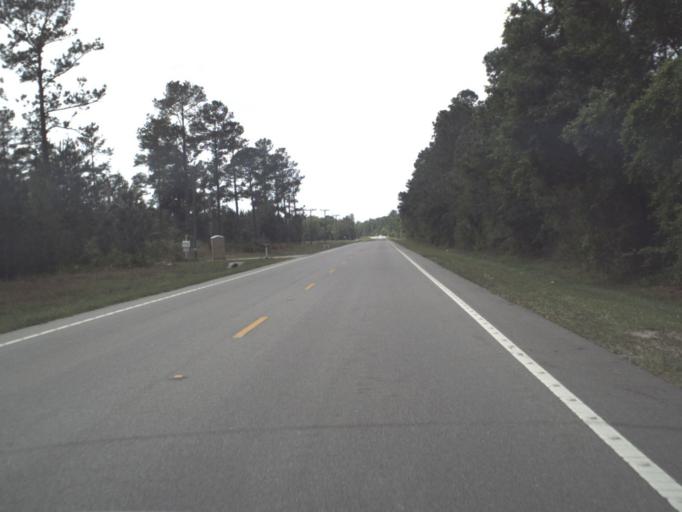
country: US
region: Florida
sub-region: Flagler County
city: Bunnell
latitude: 29.4779
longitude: -81.3370
